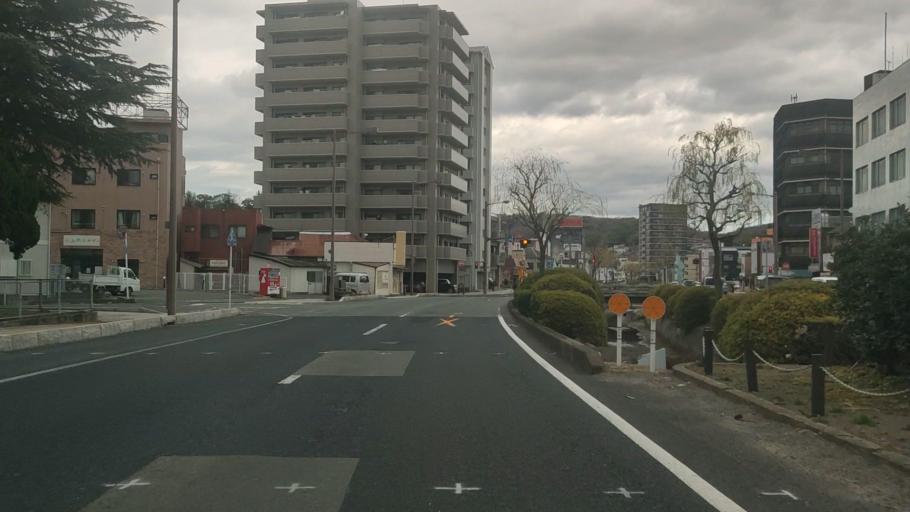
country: JP
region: Yamaguchi
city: Shimonoseki
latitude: 33.9610
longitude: 130.9416
